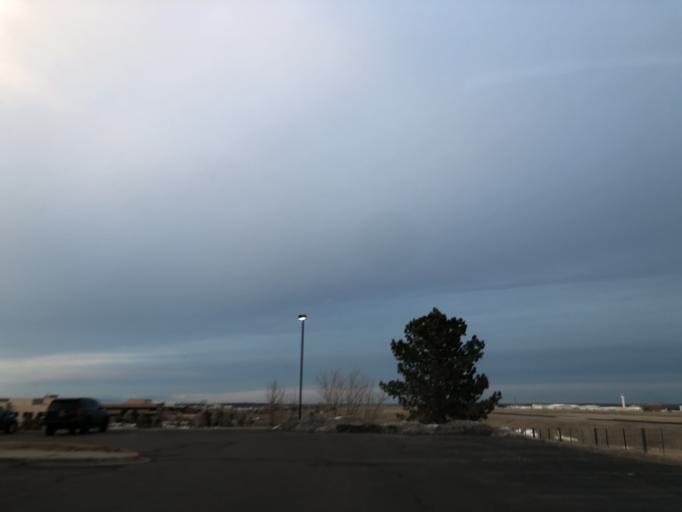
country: US
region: Colorado
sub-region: Douglas County
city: Meridian
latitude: 39.5594
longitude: -104.8548
